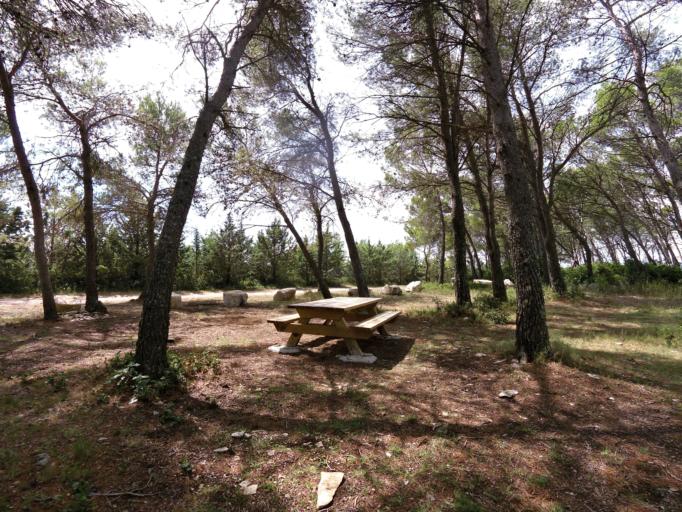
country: FR
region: Languedoc-Roussillon
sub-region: Departement du Gard
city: Calvisson
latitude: 43.7824
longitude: 4.1816
